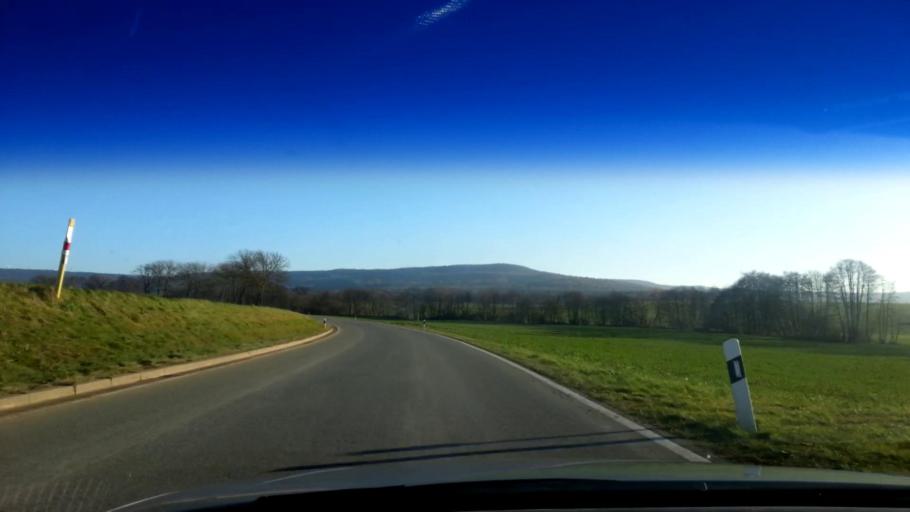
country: DE
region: Bavaria
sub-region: Upper Franconia
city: Schesslitz
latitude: 49.9572
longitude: 11.0094
